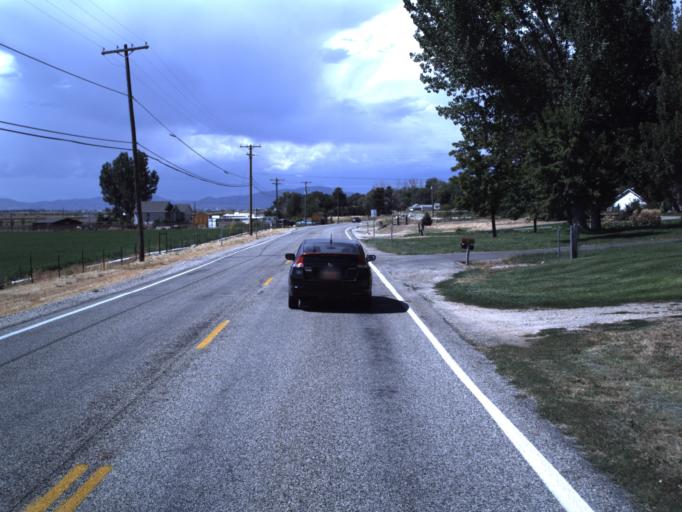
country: US
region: Utah
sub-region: Box Elder County
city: Brigham City
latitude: 41.5802
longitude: -112.0354
